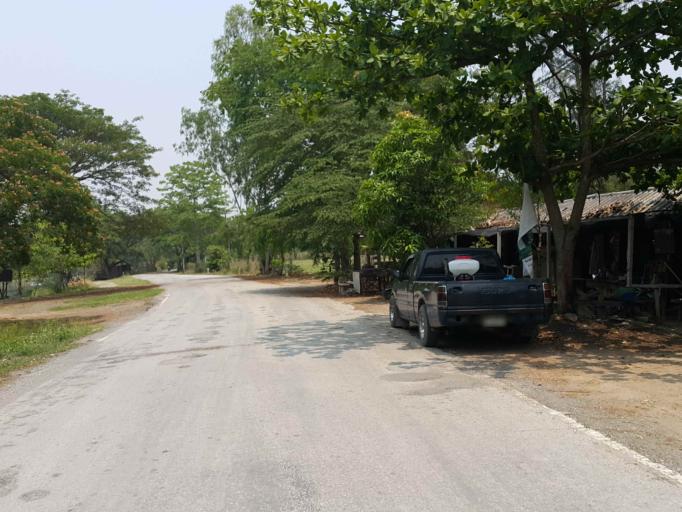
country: TH
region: Chiang Mai
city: San Sai
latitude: 18.9057
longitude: 99.0361
